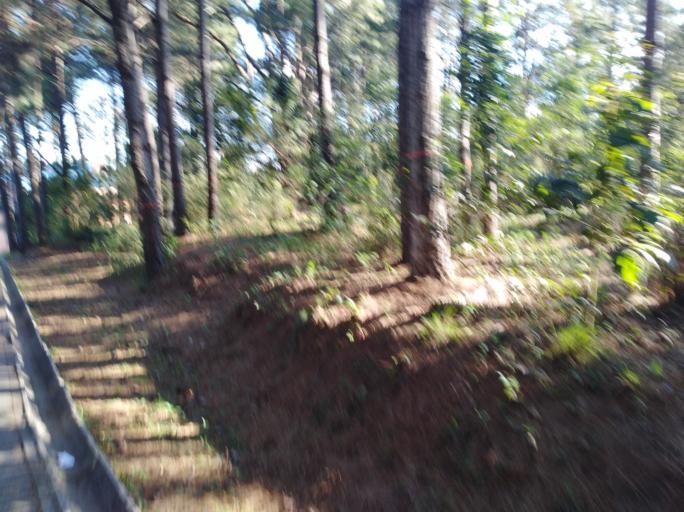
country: BR
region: Parana
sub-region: Curitiba
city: Curitiba
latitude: -25.4466
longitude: -49.2378
